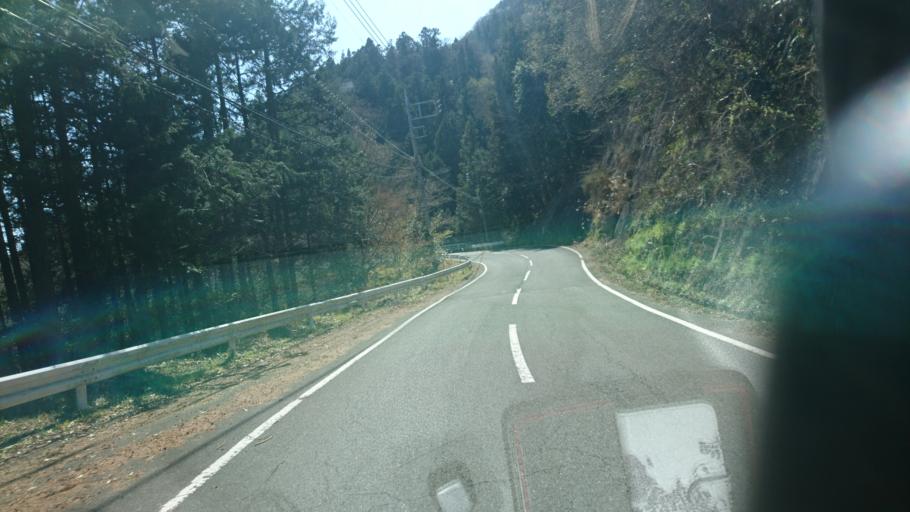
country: JP
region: Shizuoka
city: Fujinomiya
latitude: 35.3519
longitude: 138.4374
